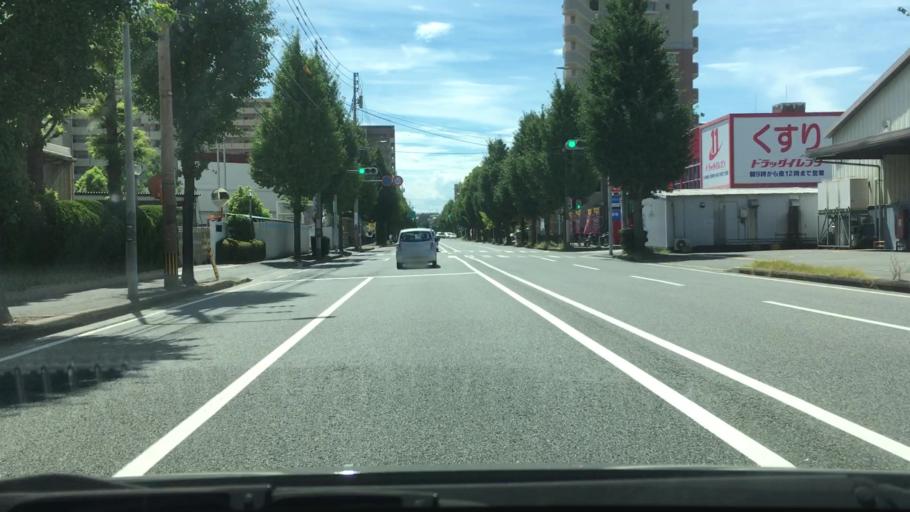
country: JP
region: Fukuoka
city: Fukuoka-shi
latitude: 33.5698
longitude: 130.4247
